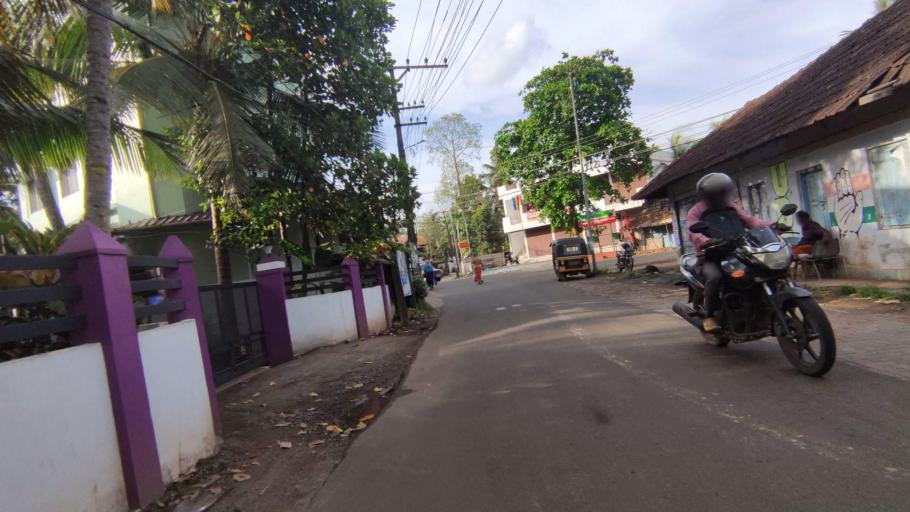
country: IN
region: Kerala
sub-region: Kottayam
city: Kottayam
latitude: 9.5849
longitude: 76.4987
